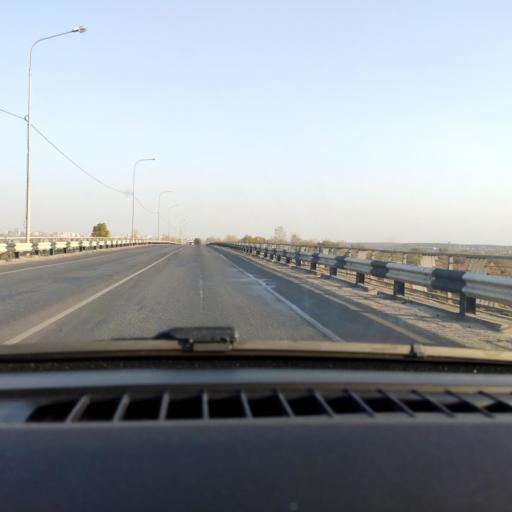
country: RU
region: Voronezj
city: Pridonskoy
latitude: 51.7242
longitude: 39.0602
